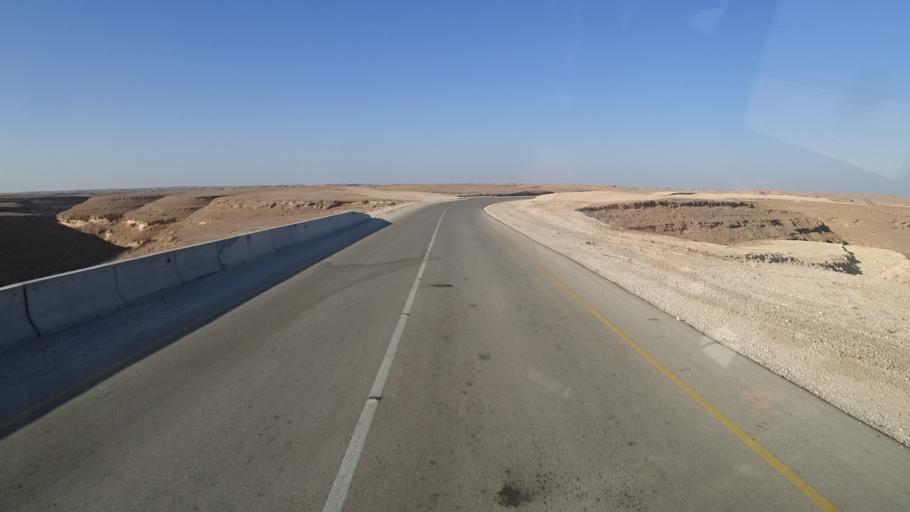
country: YE
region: Al Mahrah
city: Hawf
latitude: 17.0827
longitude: 53.0328
